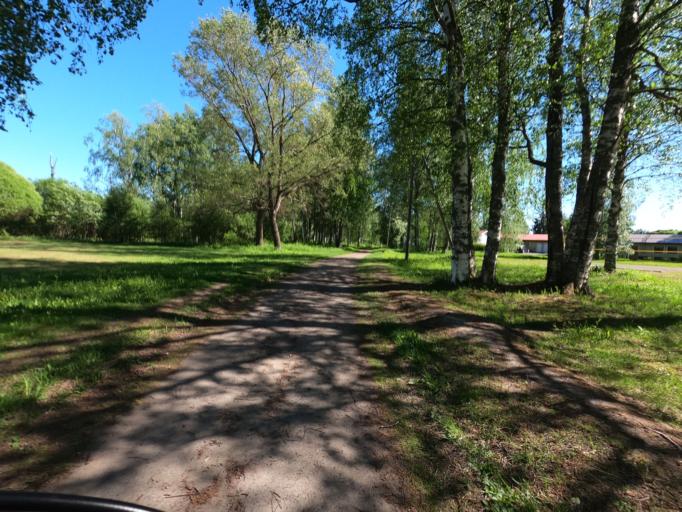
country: FI
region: North Karelia
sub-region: Joensuu
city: Joensuu
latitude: 62.6067
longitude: 29.8079
